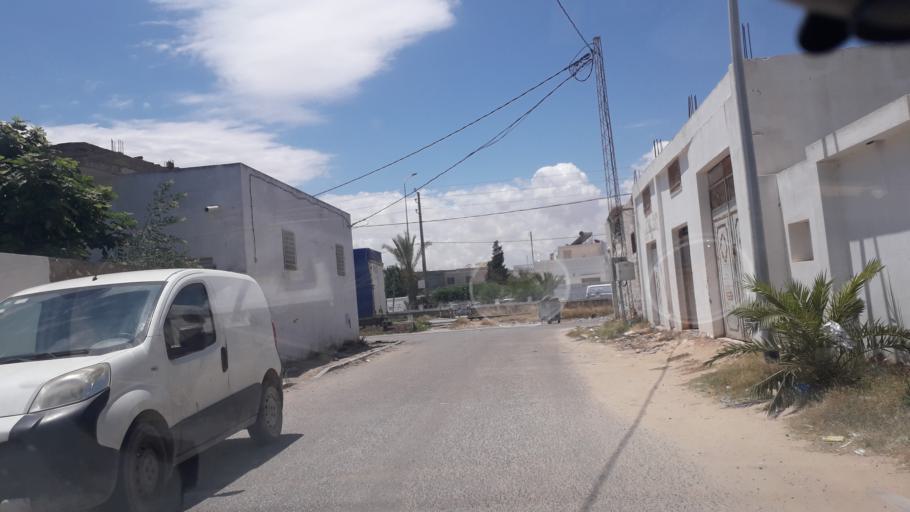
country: TN
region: Safaqis
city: Al Qarmadah
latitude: 34.8134
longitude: 10.7627
